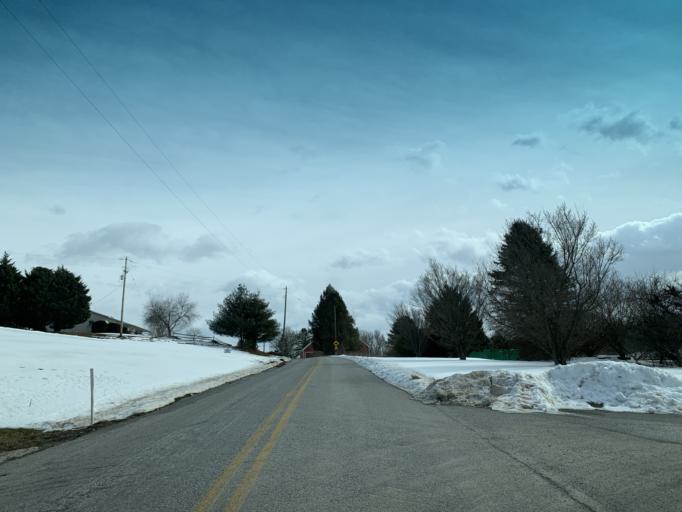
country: US
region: Pennsylvania
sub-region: York County
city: Loganville
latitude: 39.8254
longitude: -76.6819
